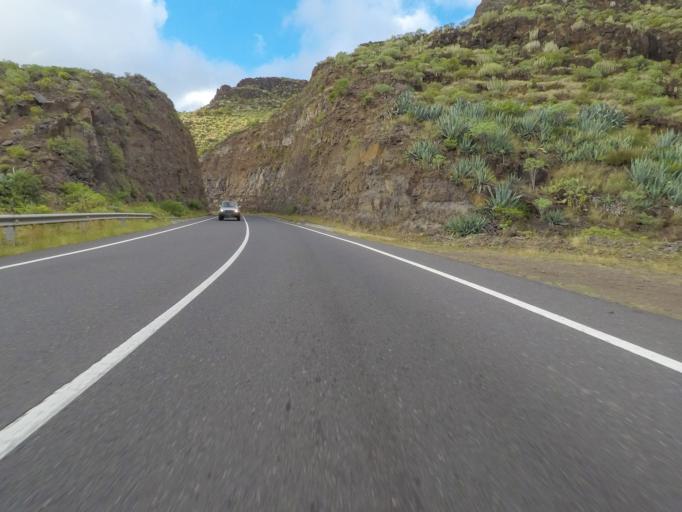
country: ES
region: Canary Islands
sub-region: Provincia de Santa Cruz de Tenerife
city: San Sebastian de la Gomera
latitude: 28.1168
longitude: -17.1389
